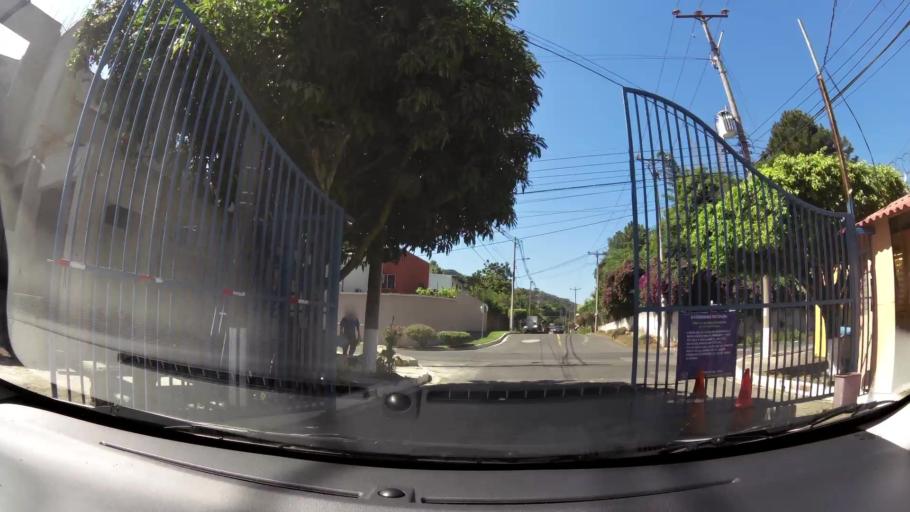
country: SV
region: La Libertad
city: Santa Tecla
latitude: 13.6662
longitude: -89.2806
